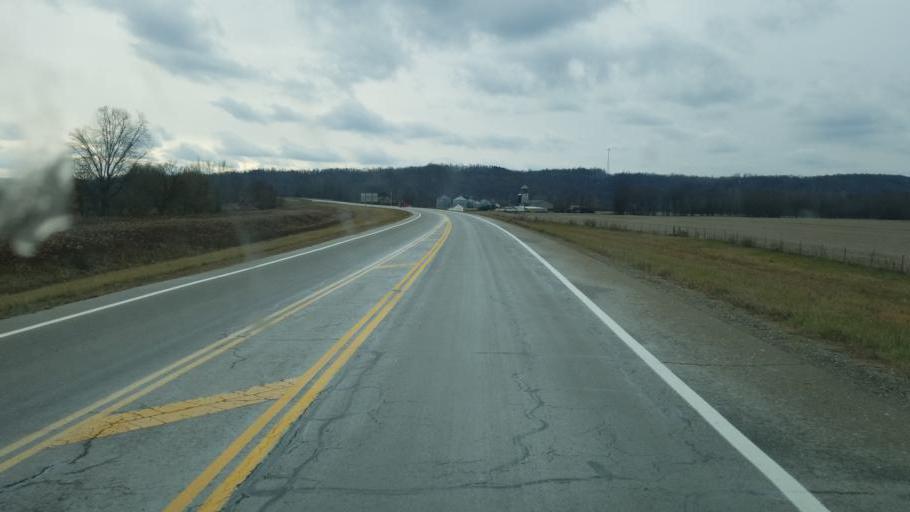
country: US
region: Ohio
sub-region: Muskingum County
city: Dresden
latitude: 40.1485
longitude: -82.0294
